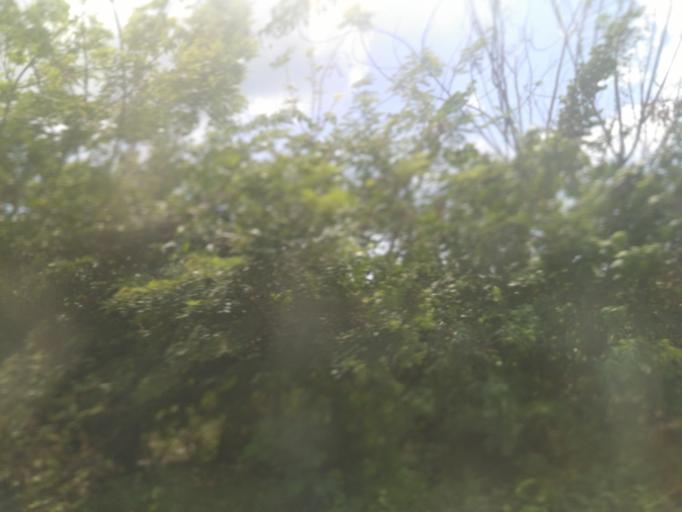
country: TZ
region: Zanzibar Urban/West
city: Zanzibar
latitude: -6.2840
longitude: 39.2821
